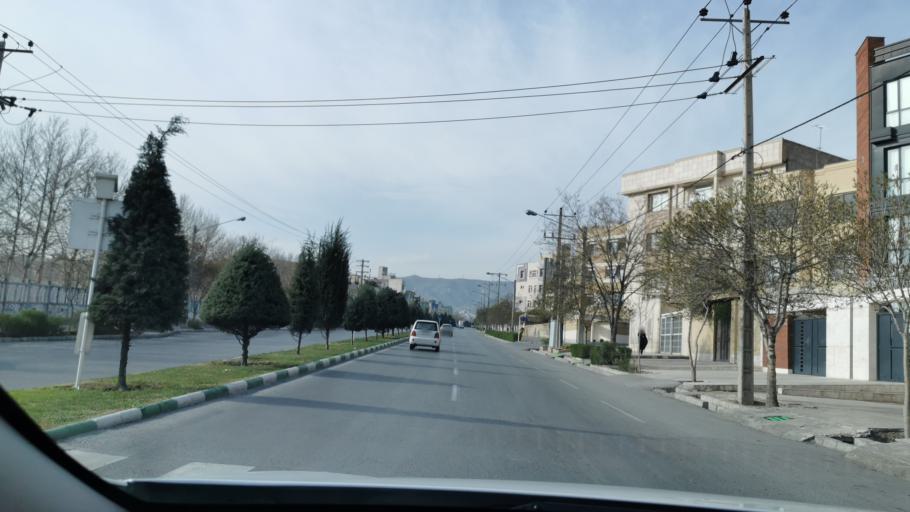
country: IR
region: Razavi Khorasan
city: Mashhad
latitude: 36.3085
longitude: 59.5147
